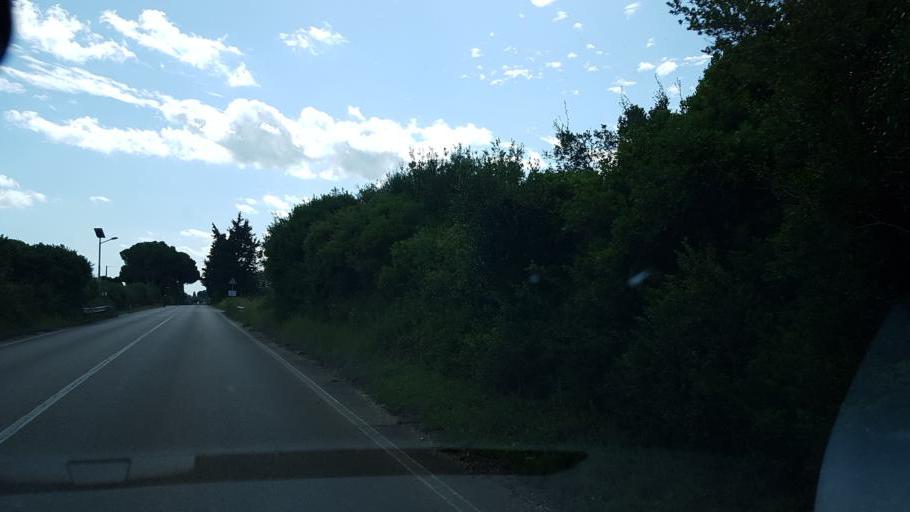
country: IT
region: Apulia
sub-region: Provincia di Lecce
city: Borgagne
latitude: 40.2365
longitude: 18.4441
